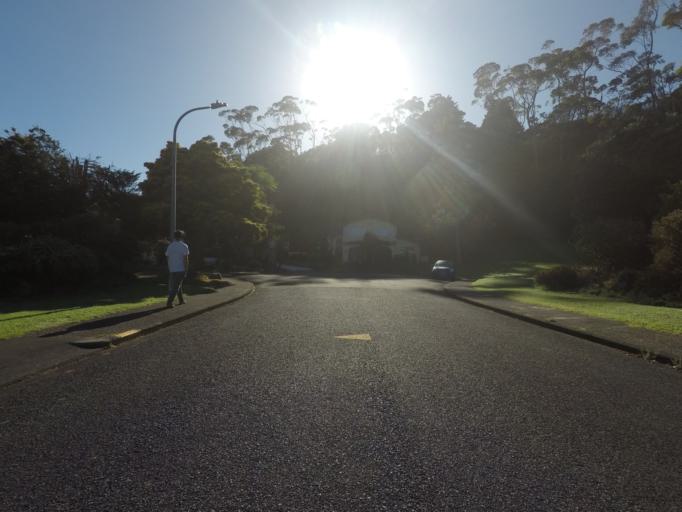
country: NZ
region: Auckland
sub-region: Auckland
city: Rosebank
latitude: -36.8919
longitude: 174.7177
